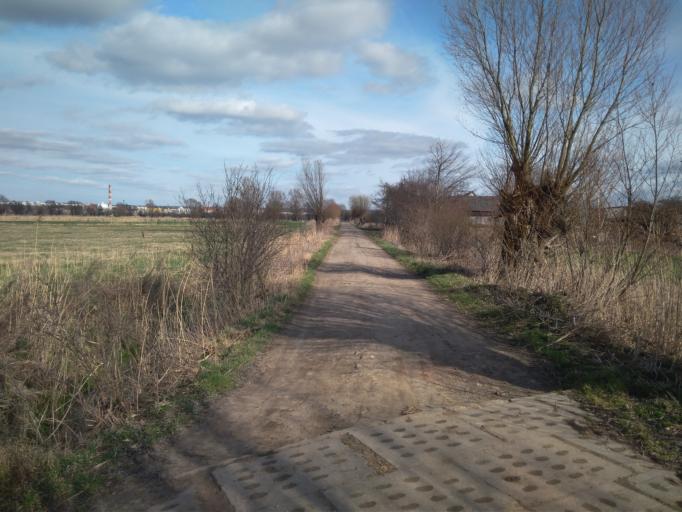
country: PL
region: Warmian-Masurian Voivodeship
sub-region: Powiat elblaski
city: Elblag
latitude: 54.1737
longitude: 19.3576
